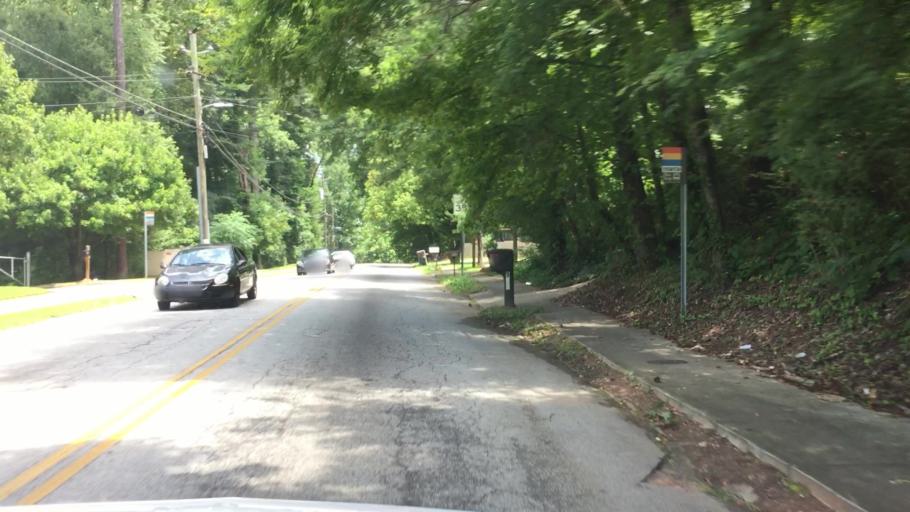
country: US
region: Georgia
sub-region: Fulton County
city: Atlanta
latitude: 33.7170
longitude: -84.3582
